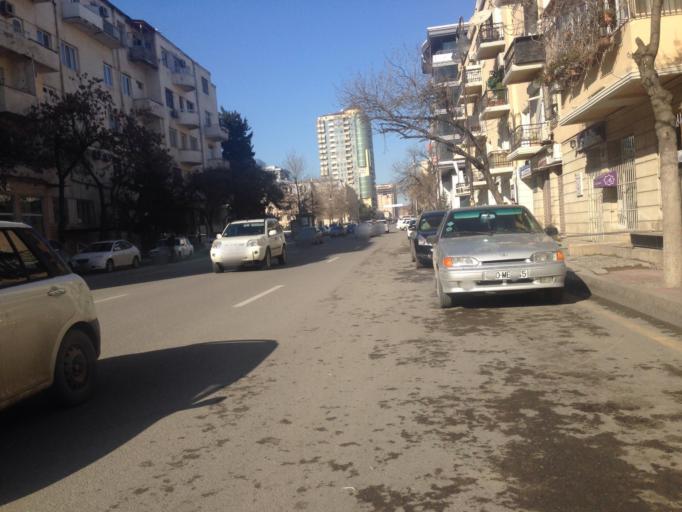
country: AZ
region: Baki
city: Baku
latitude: 40.3888
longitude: 49.8431
